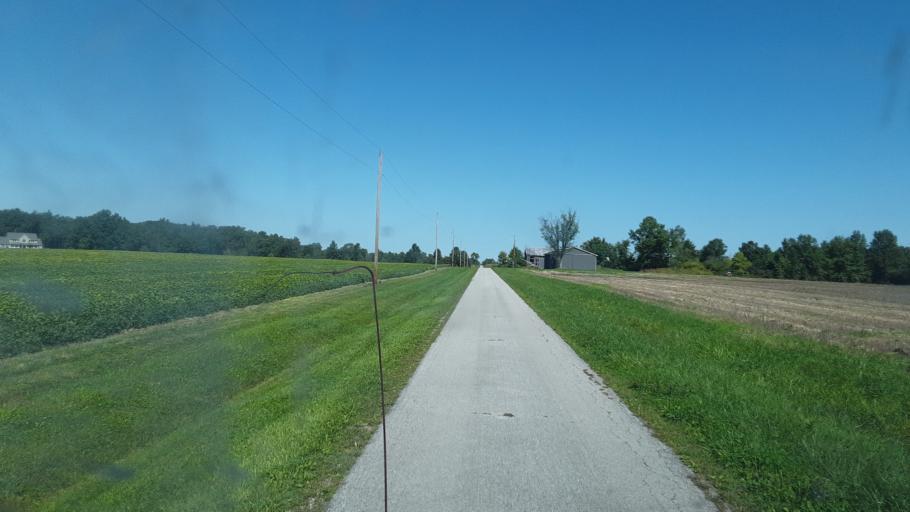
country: US
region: Ohio
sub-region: Sandusky County
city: Mount Carmel
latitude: 41.1486
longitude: -82.9189
